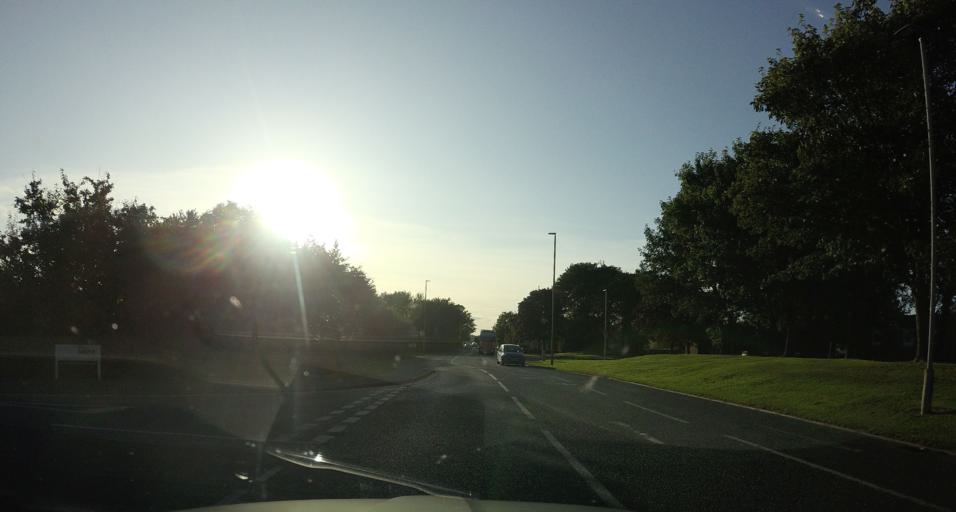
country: GB
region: Scotland
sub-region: Aberdeenshire
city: Westhill
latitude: 57.1492
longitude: -2.2906
